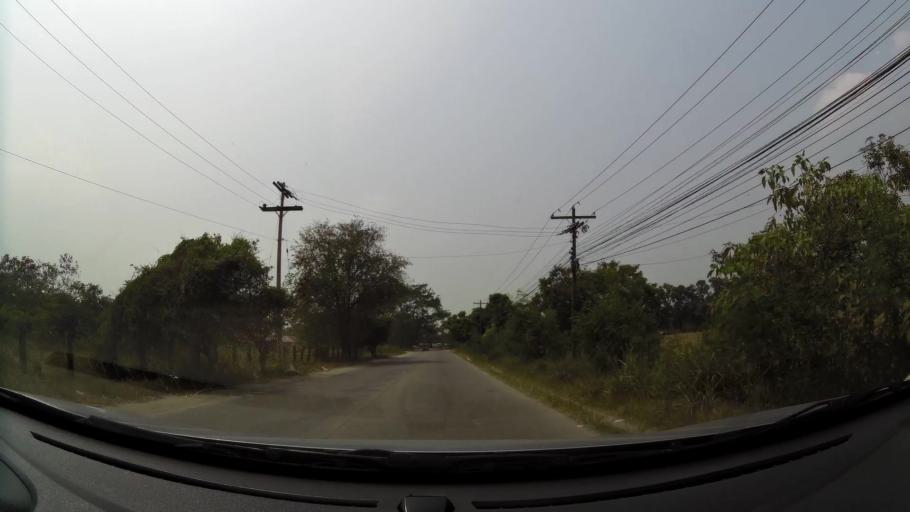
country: HN
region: Cortes
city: La Lima
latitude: 15.4351
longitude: -87.9039
